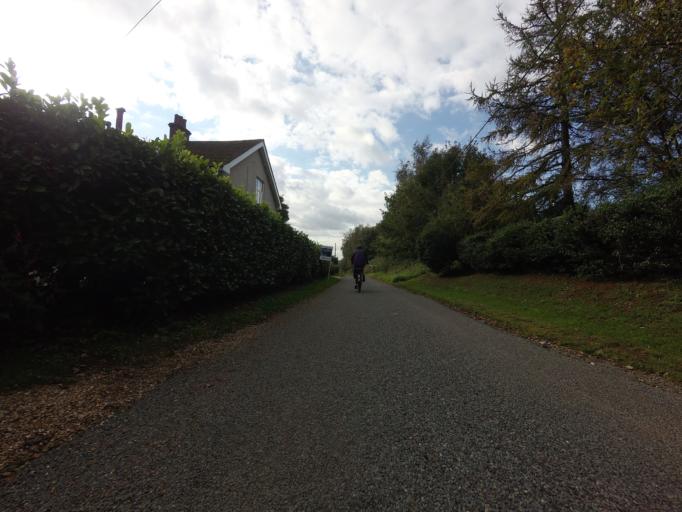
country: GB
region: England
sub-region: Norfolk
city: Dersingham
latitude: 52.8489
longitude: 0.5107
